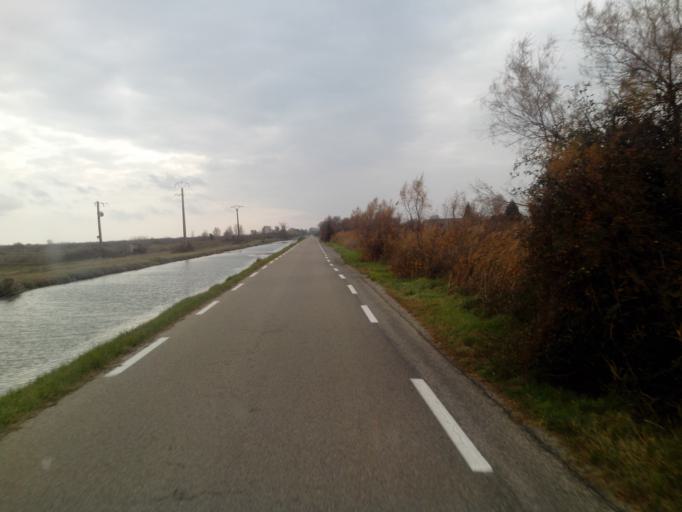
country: FR
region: Languedoc-Roussillon
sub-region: Departement du Gard
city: Vauvert
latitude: 43.6026
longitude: 4.3379
